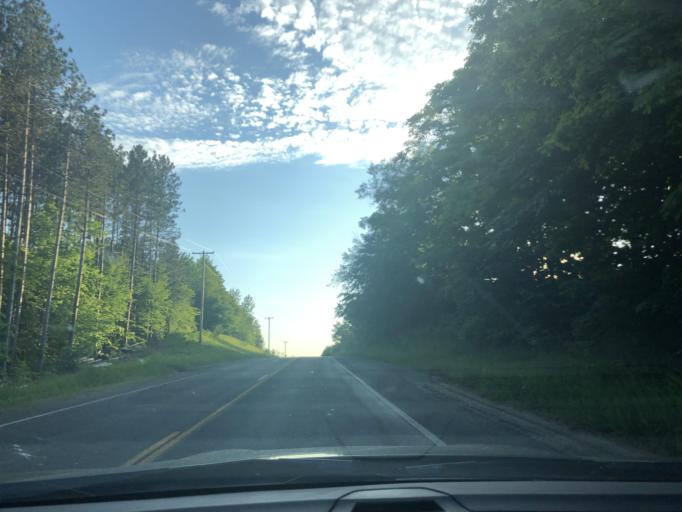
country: US
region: Michigan
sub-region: Missaukee County
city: Lake City
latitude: 44.4669
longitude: -85.1084
